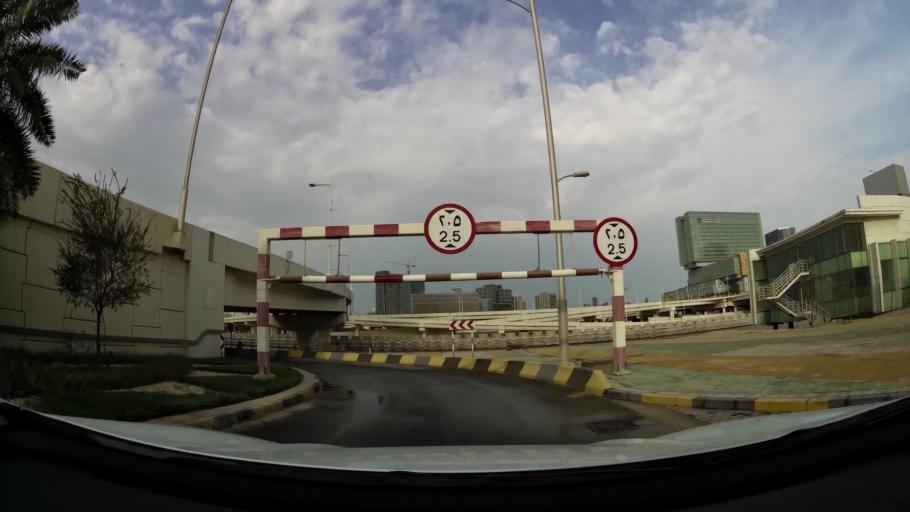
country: AE
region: Abu Dhabi
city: Abu Dhabi
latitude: 24.4937
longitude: 54.3926
